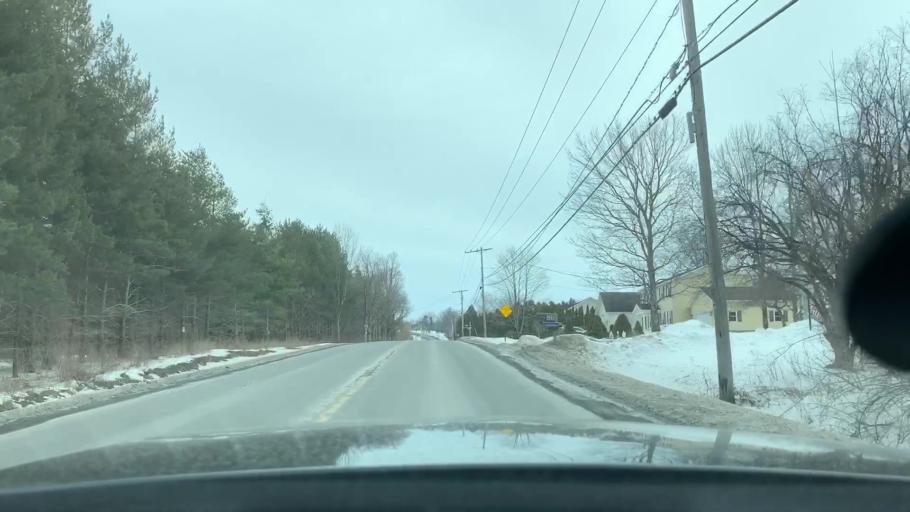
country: US
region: New York
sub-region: Oneida County
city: Washington Mills
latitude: 43.0552
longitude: -75.2461
